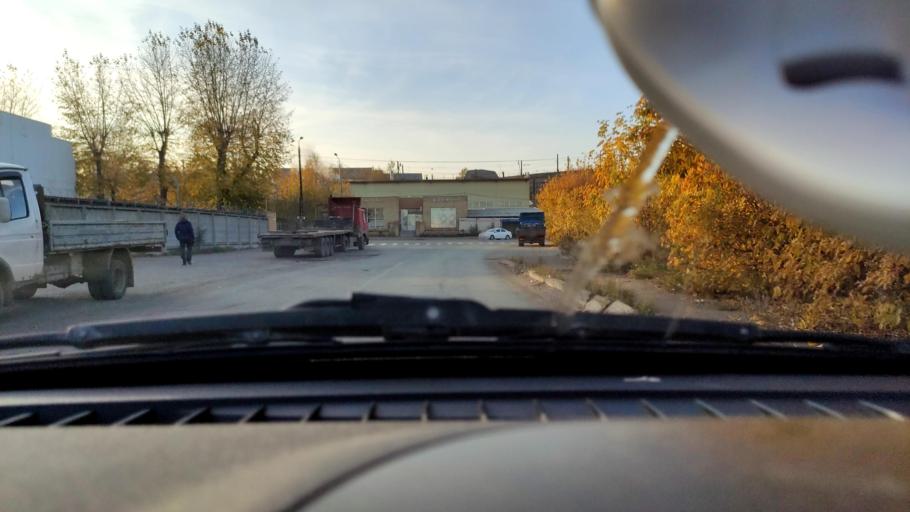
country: RU
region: Perm
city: Kondratovo
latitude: 58.0078
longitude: 56.1668
